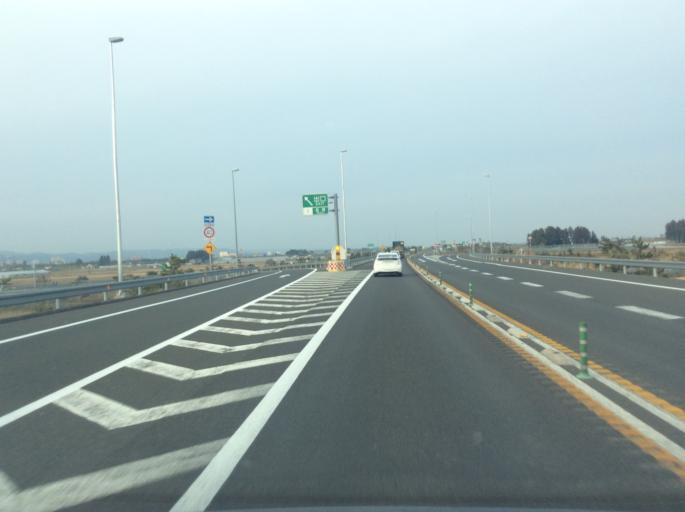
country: JP
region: Miyagi
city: Iwanuma
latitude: 38.0847
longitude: 140.8869
